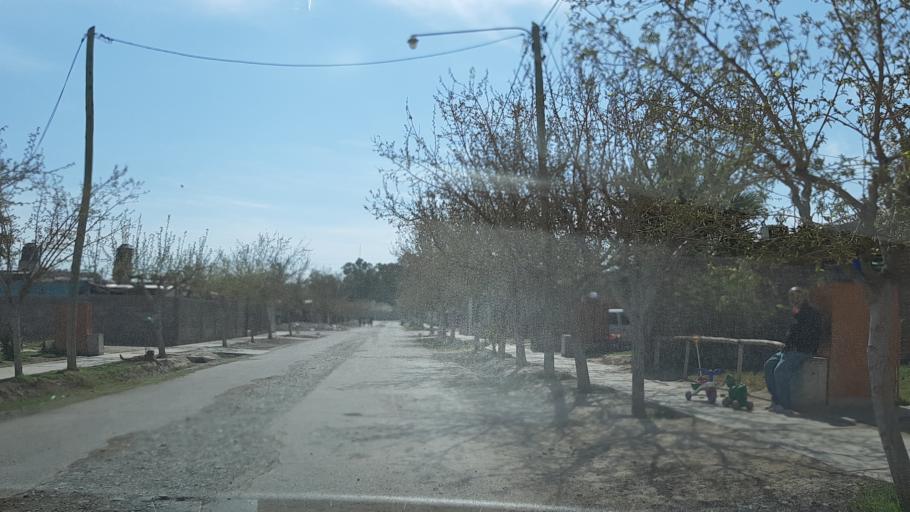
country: AR
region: San Juan
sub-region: Departamento de Zonda
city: Zonda
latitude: -31.5540
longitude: -68.7316
